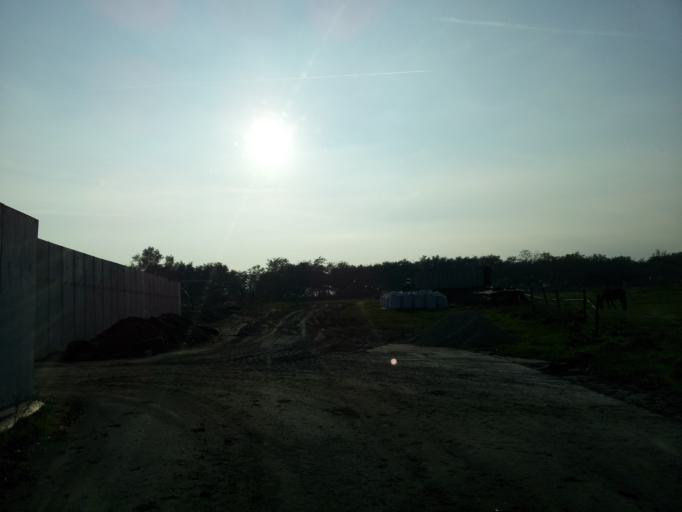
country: HU
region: Komarom-Esztergom
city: Kisber
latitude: 47.4880
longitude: 18.0473
